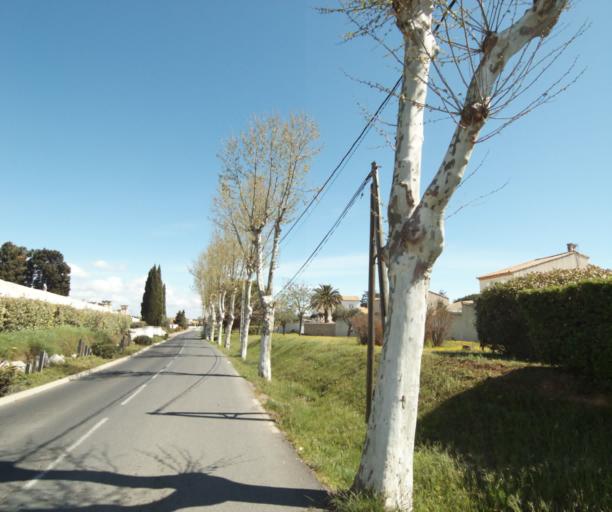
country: FR
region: Languedoc-Roussillon
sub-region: Departement de l'Herault
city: Villeneuve-les-Maguelone
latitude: 43.5349
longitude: 3.8664
